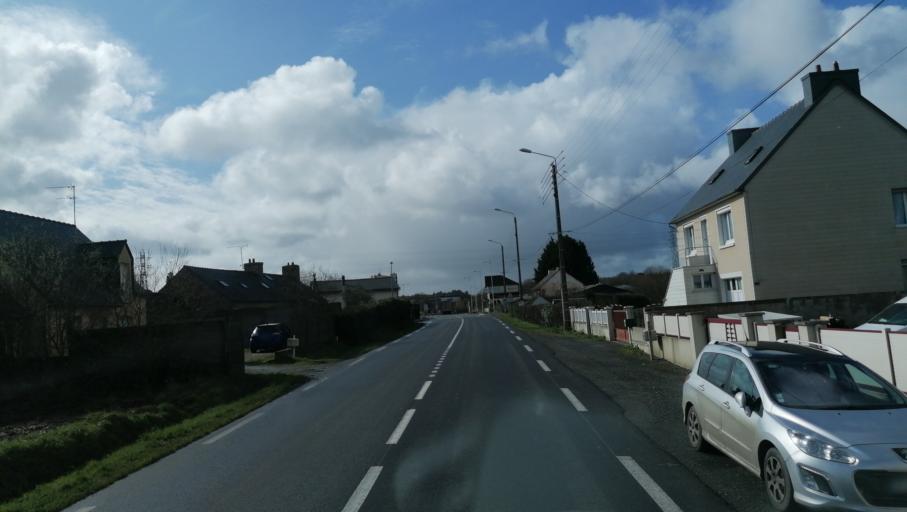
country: FR
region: Brittany
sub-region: Departement des Cotes-d'Armor
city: Ploufragan
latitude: 48.4735
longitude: -2.8006
